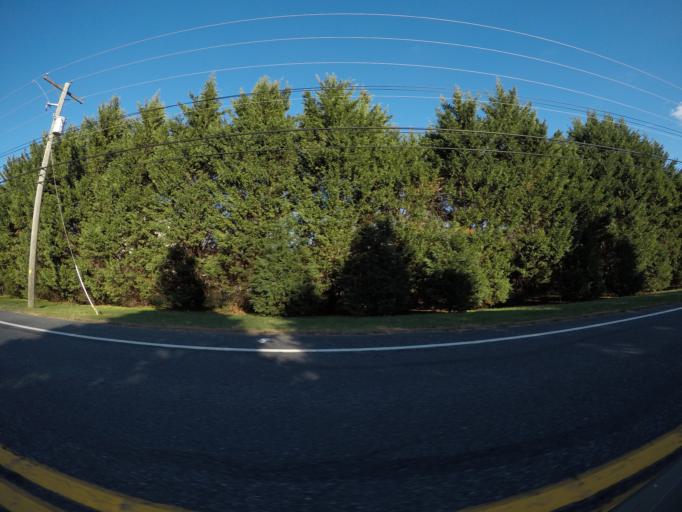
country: US
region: Maryland
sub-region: Harford County
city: South Bel Air
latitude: 39.6264
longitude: -76.2621
